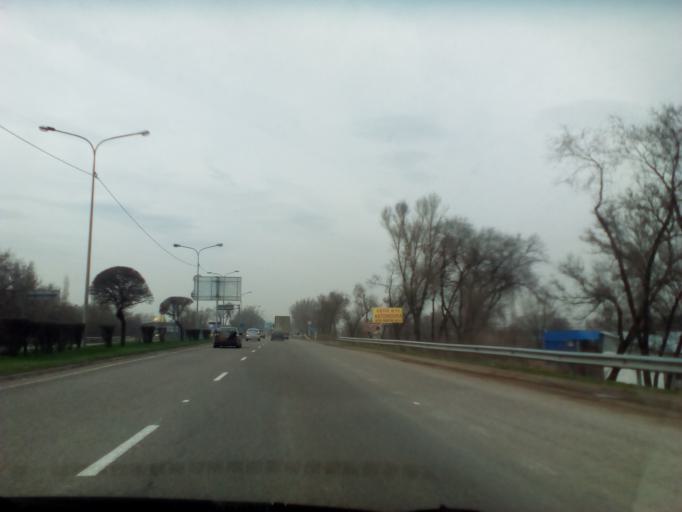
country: KZ
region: Almaty Oblysy
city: Burunday
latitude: 43.2189
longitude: 76.6431
